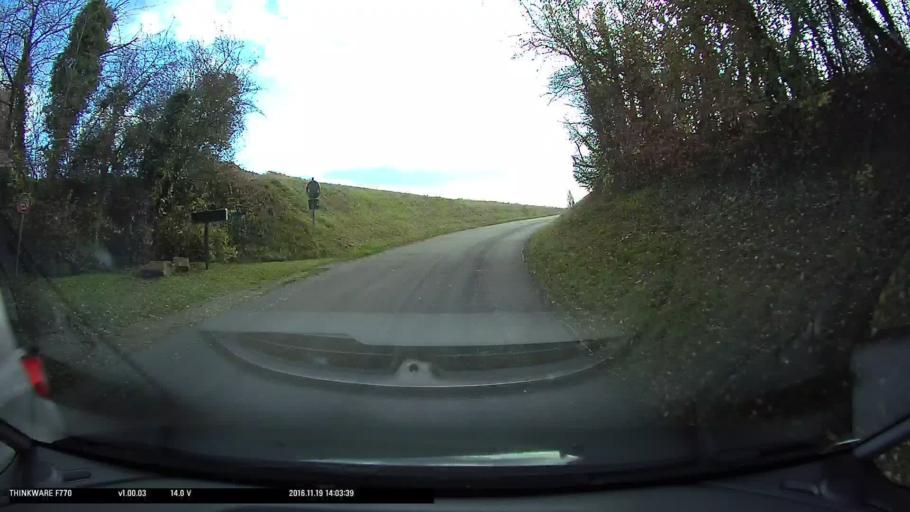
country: FR
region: Ile-de-France
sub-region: Departement du Val-d'Oise
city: Ableiges
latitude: 49.0724
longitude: 2.0051
